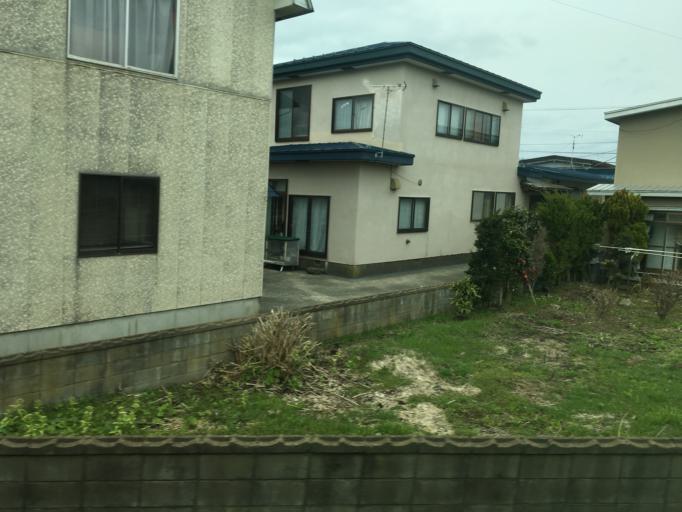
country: JP
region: Aomori
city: Shimokizukuri
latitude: 40.7791
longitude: 140.2248
